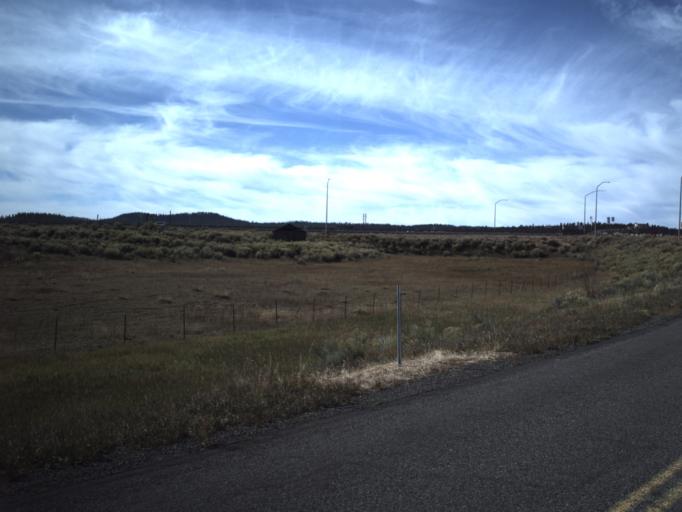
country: US
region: Utah
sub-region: Garfield County
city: Panguitch
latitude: 37.6941
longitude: -112.1505
